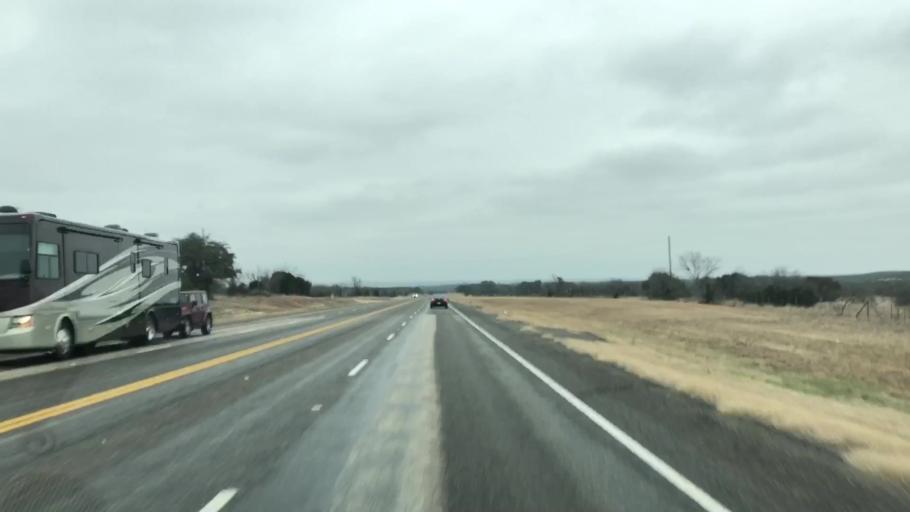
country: US
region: Texas
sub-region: Lampasas County
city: Lampasas
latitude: 31.0014
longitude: -98.1944
